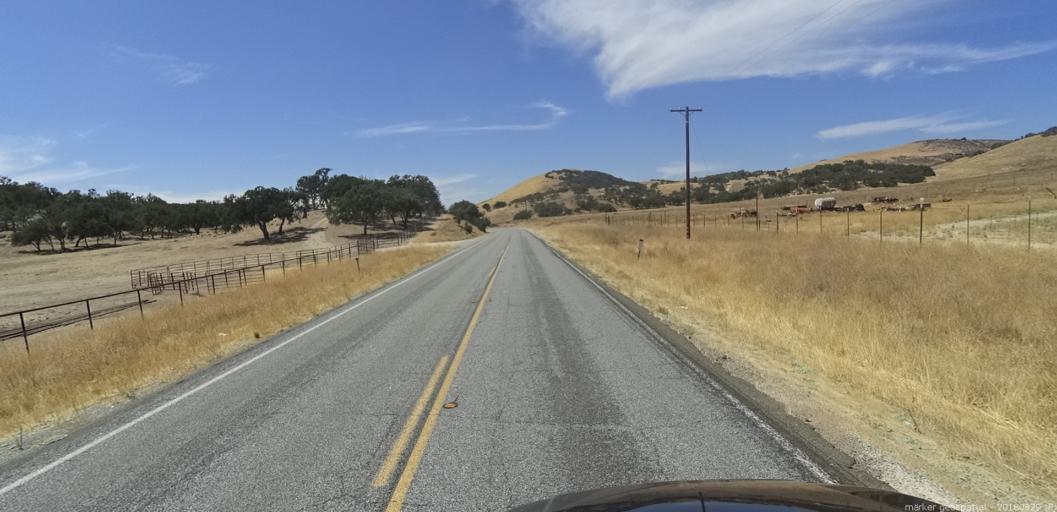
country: US
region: California
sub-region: San Luis Obispo County
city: Lake Nacimiento
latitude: 35.9074
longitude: -121.0012
